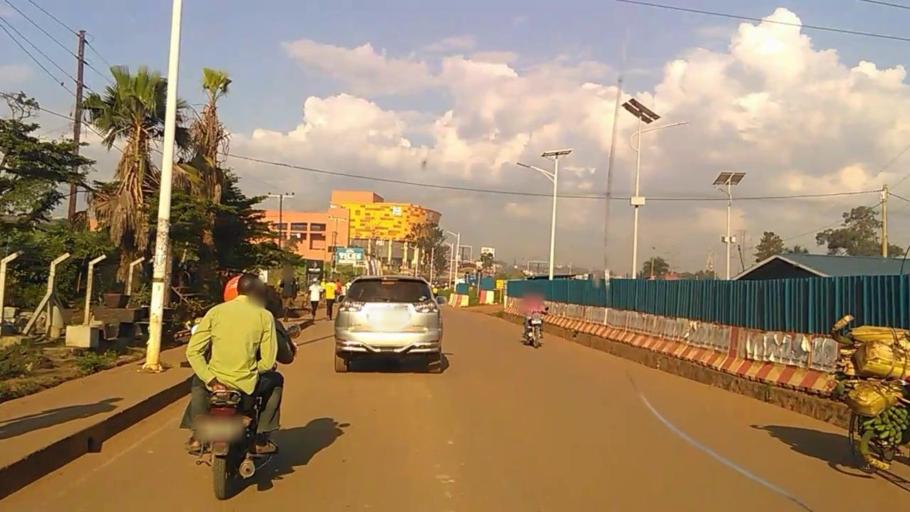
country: UG
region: Central Region
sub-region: Kampala District
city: Kampala
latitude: 0.3080
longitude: 32.5879
